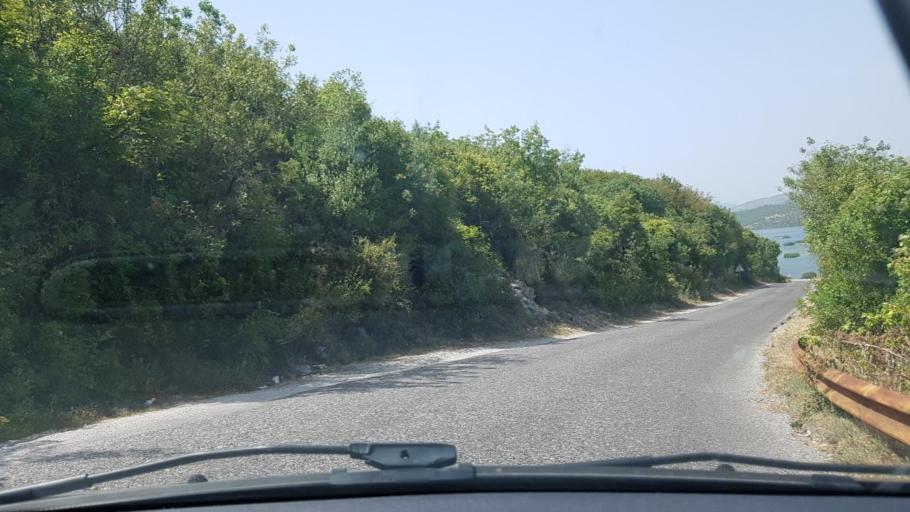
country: BA
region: Federation of Bosnia and Herzegovina
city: Tasovcici
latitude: 43.0155
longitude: 17.7835
